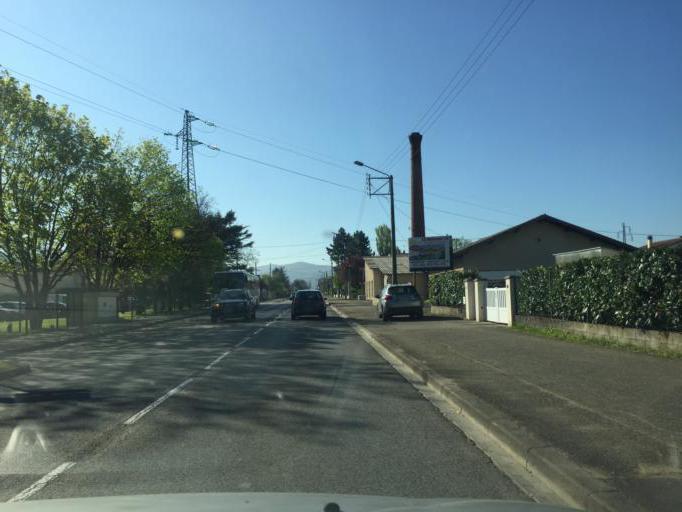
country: FR
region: Rhone-Alpes
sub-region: Departement de l'Ain
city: Amberieu-en-Bugey
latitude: 45.9719
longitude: 5.3523
